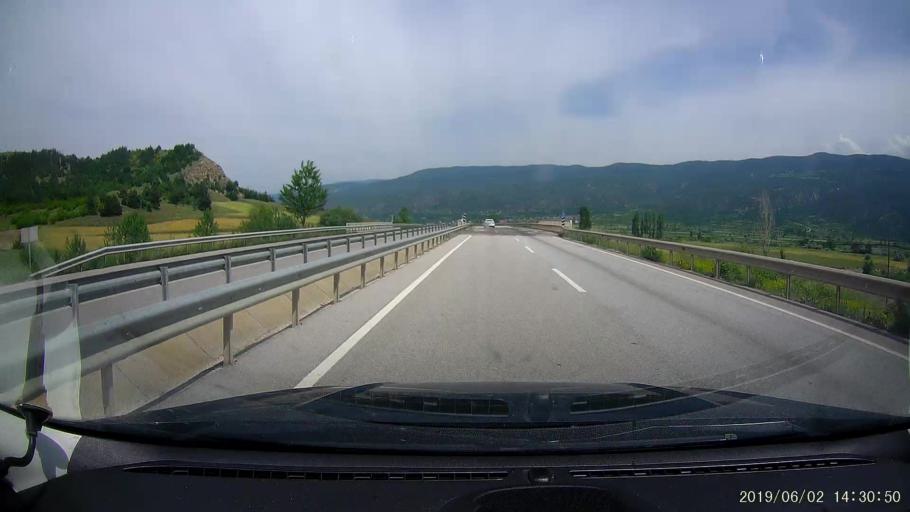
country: TR
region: Kastamonu
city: Tosya
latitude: 41.0154
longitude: 34.1243
